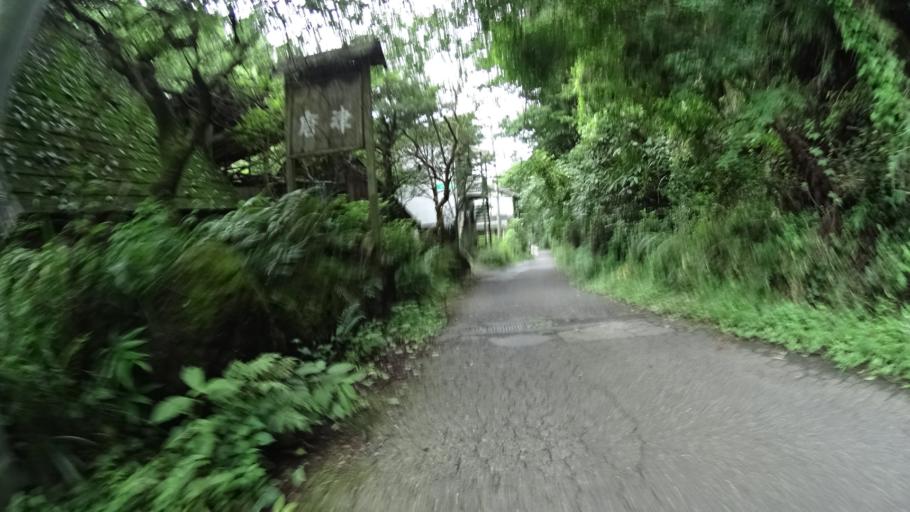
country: JP
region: Kanagawa
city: Atsugi
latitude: 35.4995
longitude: 139.2657
